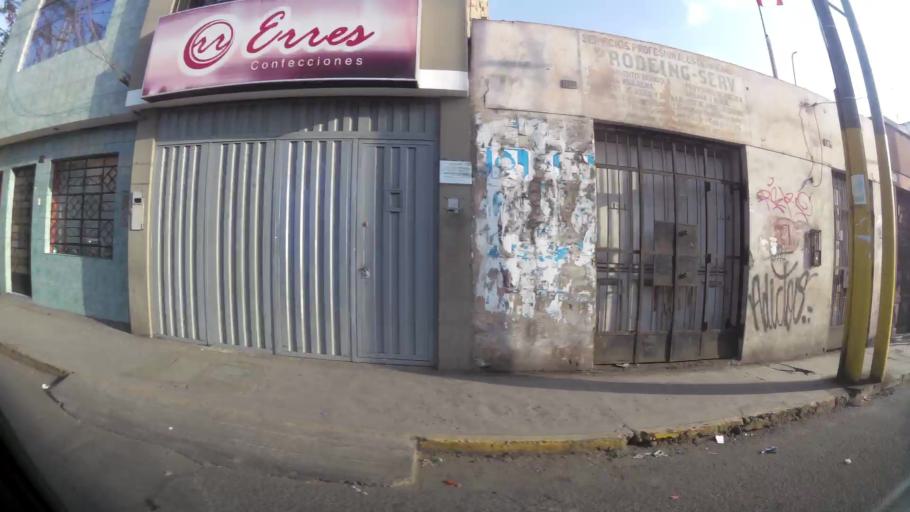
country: PE
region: Lima
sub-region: Huaura
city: Huacho
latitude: -11.1054
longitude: -77.6067
